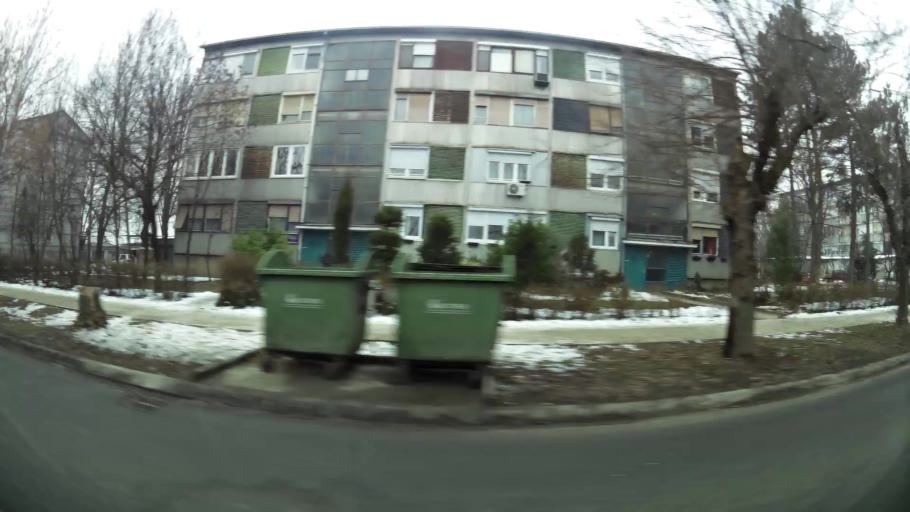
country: MK
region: Cair
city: Cair
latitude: 42.0121
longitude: 21.4586
